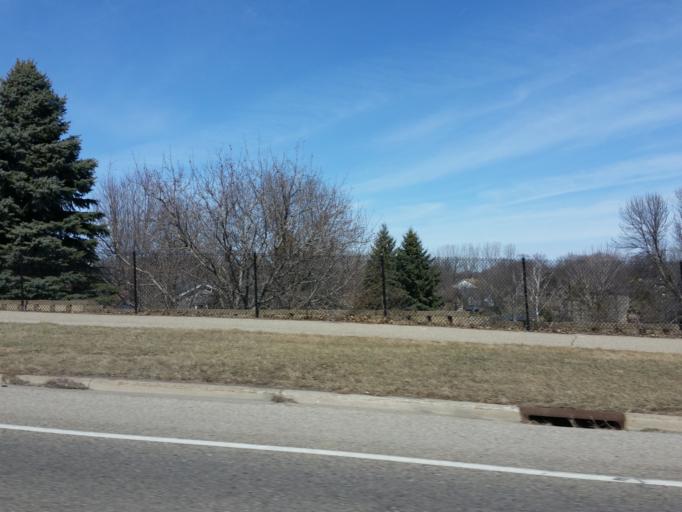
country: US
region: Minnesota
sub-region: Dakota County
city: Eagan
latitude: 44.7902
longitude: -93.1508
